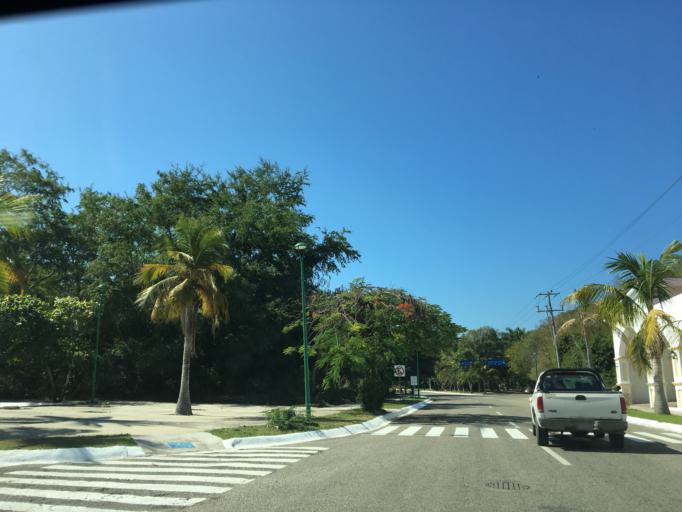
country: MX
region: Oaxaca
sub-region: Santa Maria Huatulco
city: Crucecita
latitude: 15.7757
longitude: -96.0979
